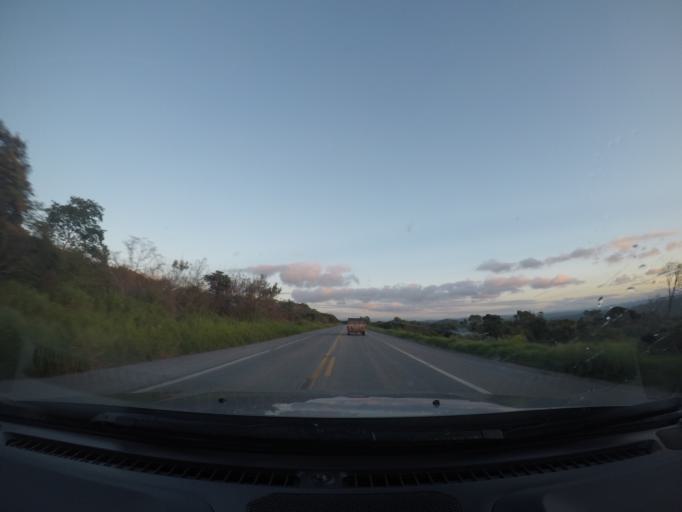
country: BR
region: Bahia
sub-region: Seabra
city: Seabra
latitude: -12.4291
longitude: -41.8284
